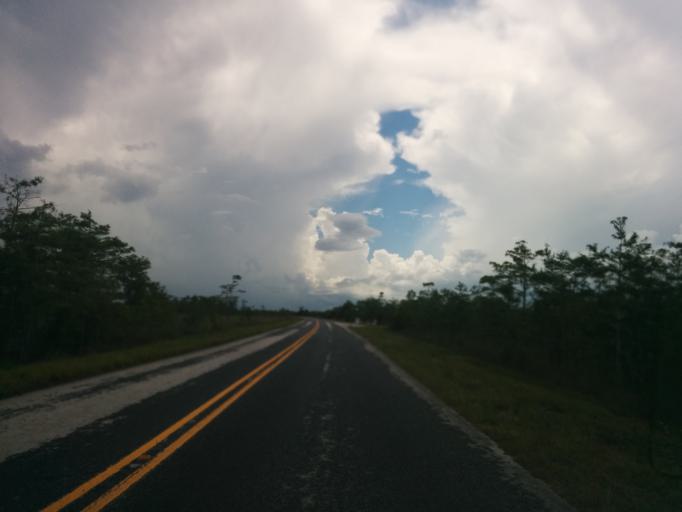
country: US
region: Florida
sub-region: Miami-Dade County
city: Florida City
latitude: 25.4338
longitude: -80.7523
